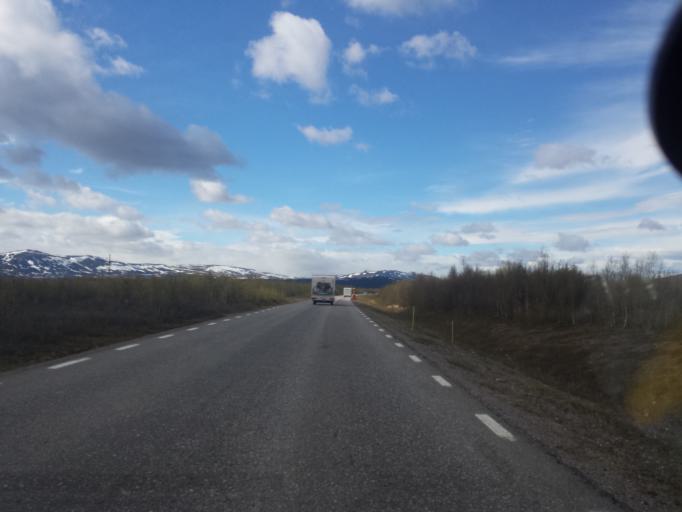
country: SE
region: Norrbotten
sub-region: Kiruna Kommun
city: Kiruna
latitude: 68.0035
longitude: 19.8542
